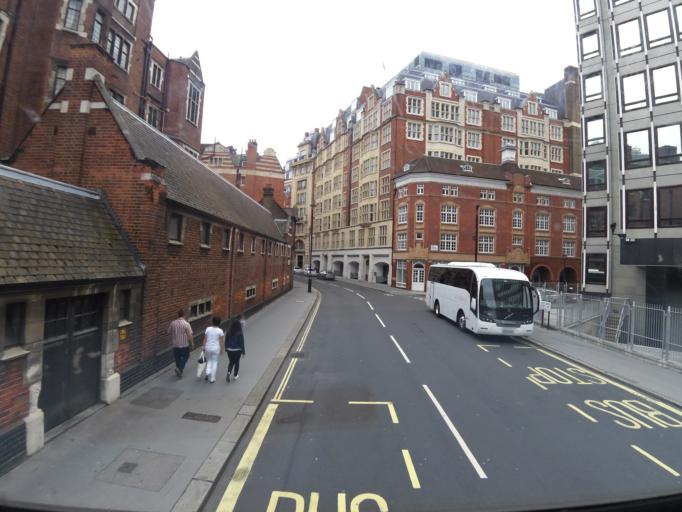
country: GB
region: England
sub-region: Greater London
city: London
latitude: 51.4987
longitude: -0.1299
